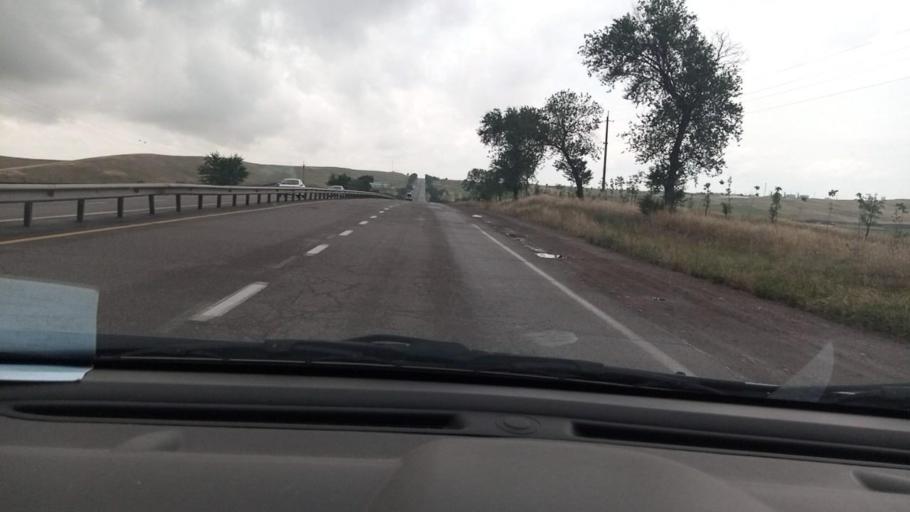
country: UZ
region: Toshkent
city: Ohangaron
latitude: 40.9483
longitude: 69.5733
